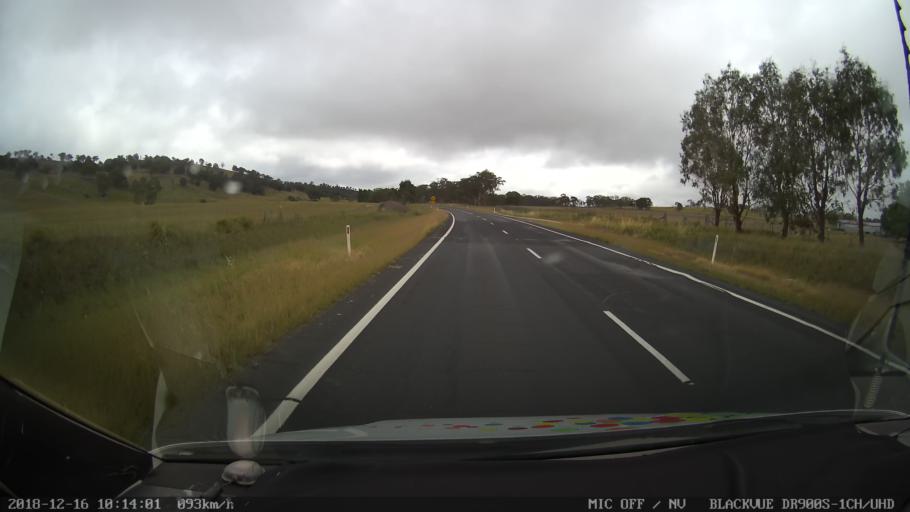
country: AU
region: New South Wales
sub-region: Tenterfield Municipality
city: Carrolls Creek
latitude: -29.2917
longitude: 151.9591
